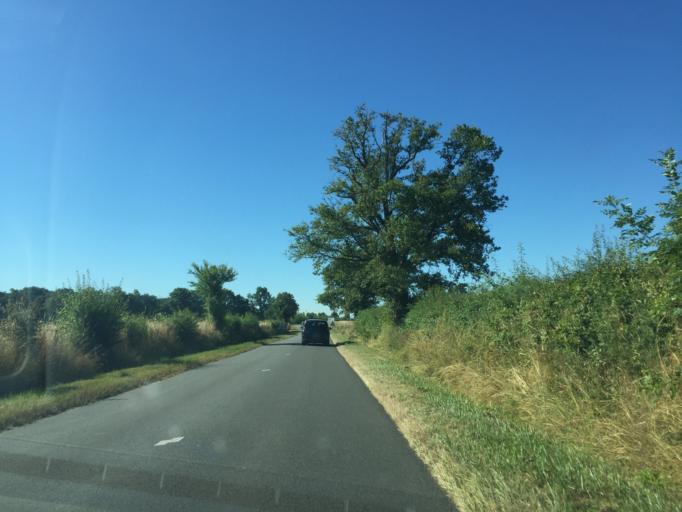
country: FR
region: Auvergne
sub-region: Departement de l'Allier
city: Dompierre-sur-Besbre
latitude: 46.5158
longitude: 3.6218
